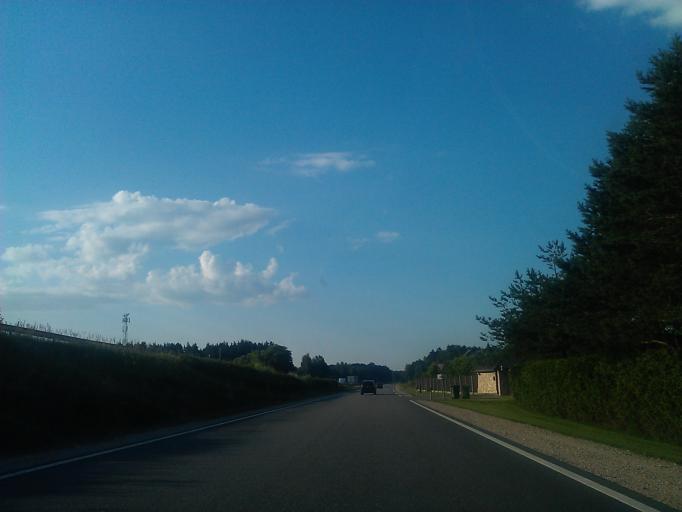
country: LV
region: Babite
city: Pinki
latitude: 56.9249
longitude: 23.9152
